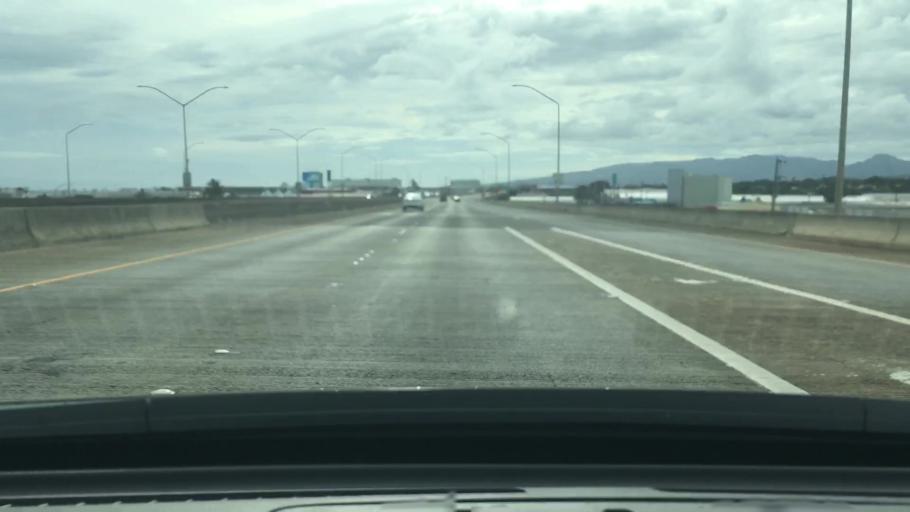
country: US
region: Hawaii
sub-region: Honolulu County
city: Halawa Heights
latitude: 21.3352
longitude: -157.8967
